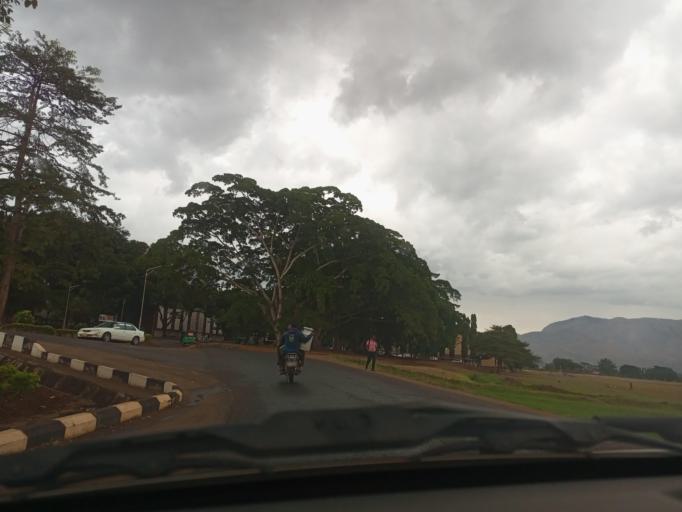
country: TZ
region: Morogoro
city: Morogoro
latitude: -6.8517
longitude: 37.6572
